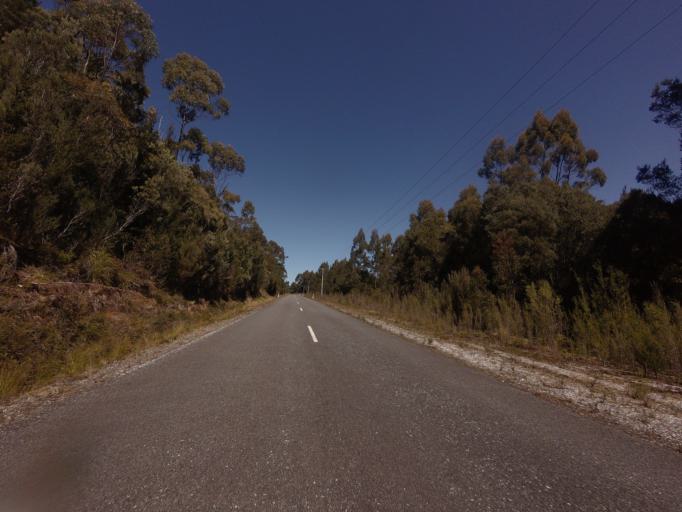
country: AU
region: Tasmania
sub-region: West Coast
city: Queenstown
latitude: -42.7787
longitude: 146.0294
